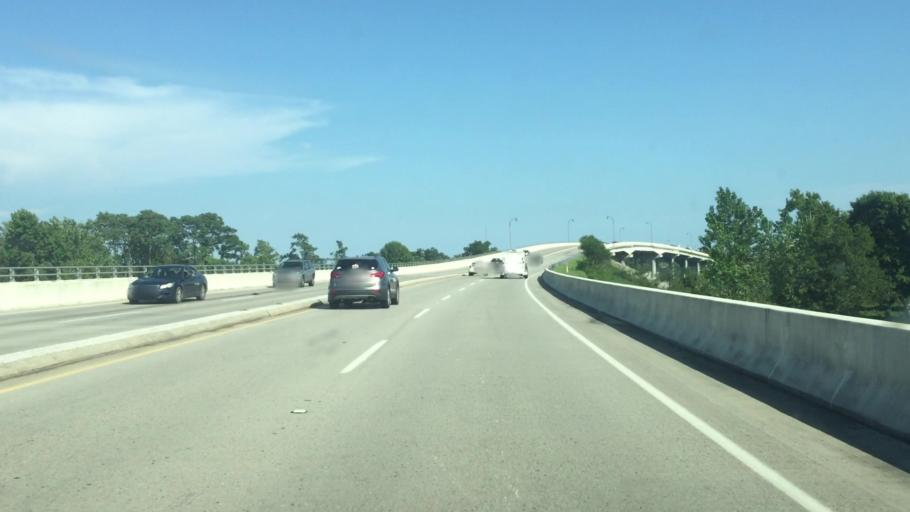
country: US
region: South Carolina
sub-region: Horry County
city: North Myrtle Beach
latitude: 33.8363
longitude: -78.6873
